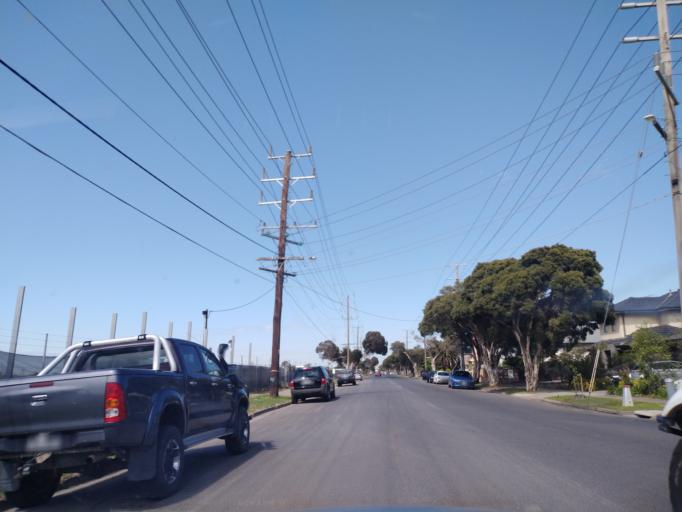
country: AU
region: Victoria
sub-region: Hobsons Bay
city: Altona North
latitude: -37.8279
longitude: 144.8571
